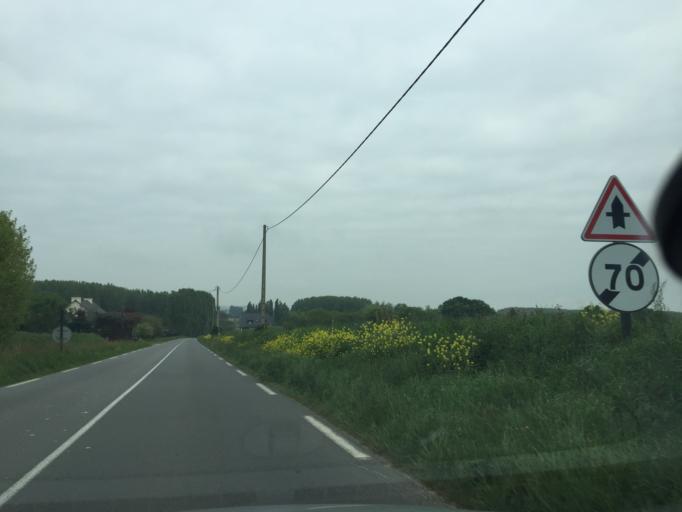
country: FR
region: Brittany
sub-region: Departement des Cotes-d'Armor
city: Matignon
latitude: 48.5880
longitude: -2.3168
